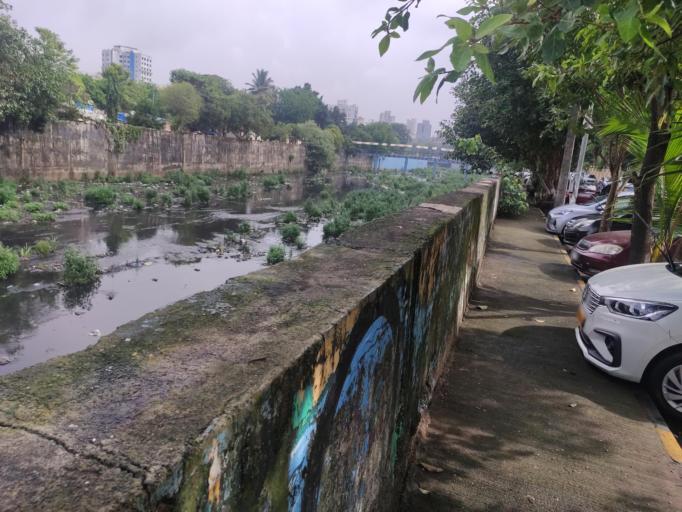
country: IN
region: Maharashtra
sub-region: Mumbai Suburban
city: Borivli
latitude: 19.2447
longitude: 72.8572
